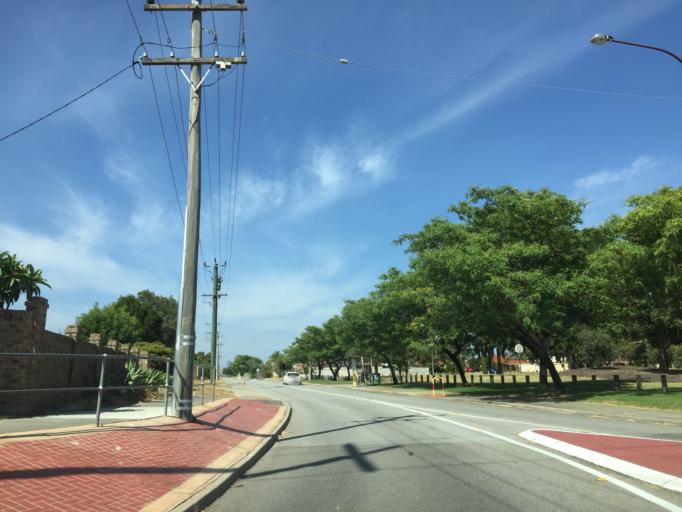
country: AU
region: Western Australia
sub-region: Gosnells
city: Thornlie
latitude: -32.0784
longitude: 115.9649
